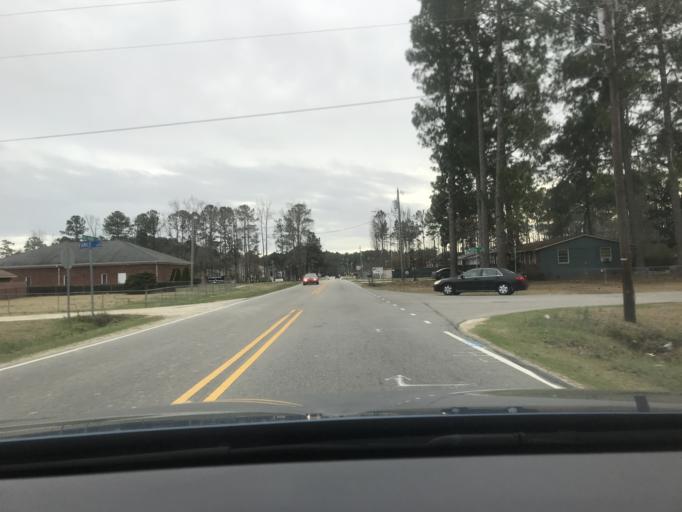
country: US
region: North Carolina
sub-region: Hoke County
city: Rockfish
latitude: 35.0557
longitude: -79.0119
